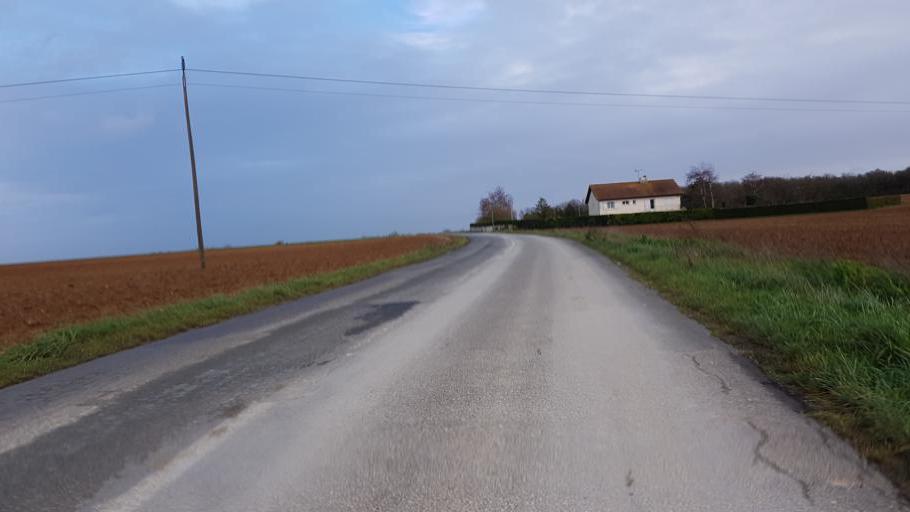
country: FR
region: Poitou-Charentes
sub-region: Departement de la Vienne
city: Avanton
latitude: 46.6618
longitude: 0.3182
